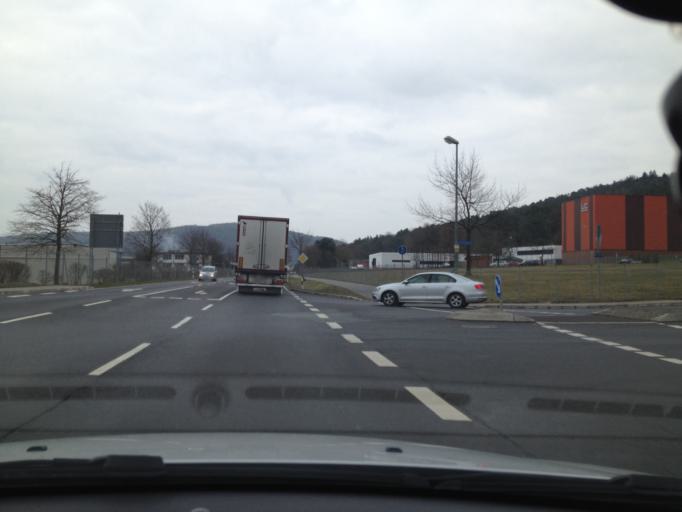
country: DE
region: Bavaria
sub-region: Regierungsbezirk Unterfranken
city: Hasloch
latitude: 49.7793
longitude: 9.4782
